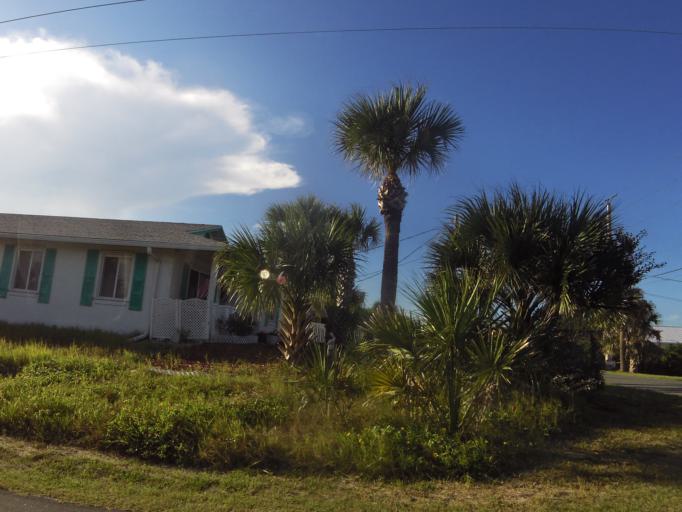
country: US
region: Florida
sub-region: Flagler County
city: Flagler Beach
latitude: 29.4534
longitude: -81.1154
